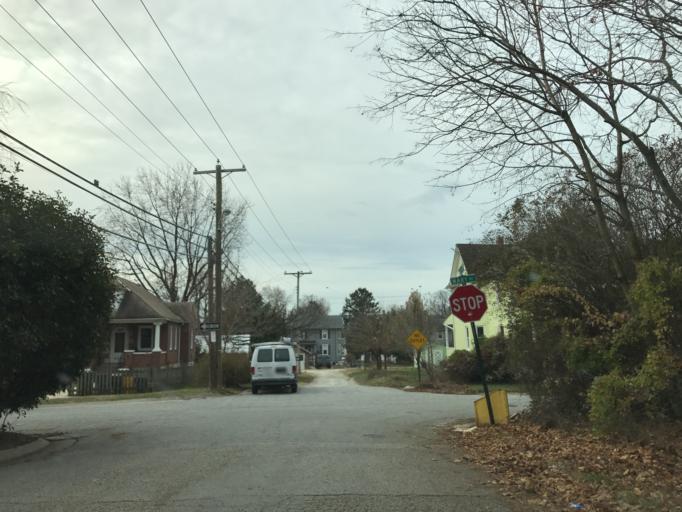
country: US
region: Maryland
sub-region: Baltimore County
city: Overlea
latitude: 39.3435
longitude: -76.5379
